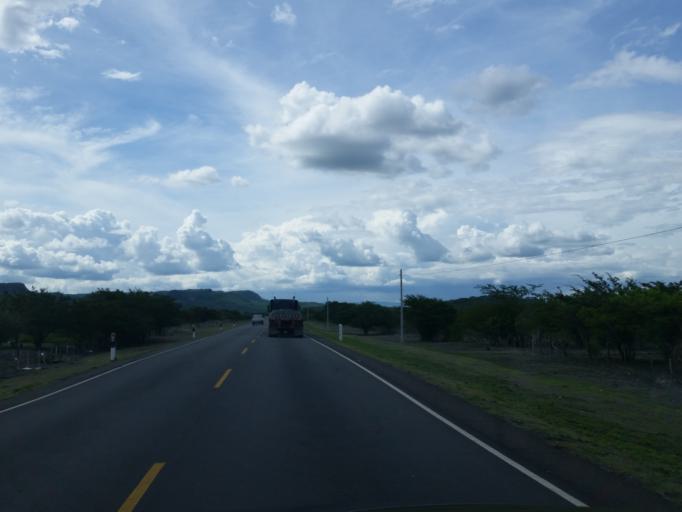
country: NI
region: Matagalpa
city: Ciudad Dario
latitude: 12.6542
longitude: -86.0767
